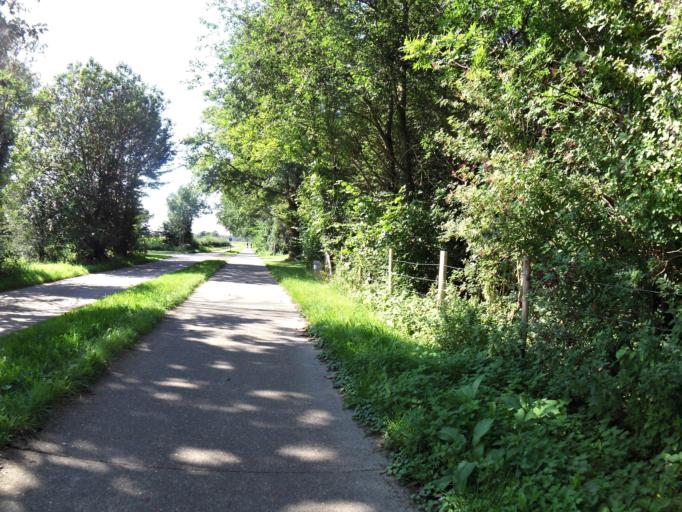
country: BE
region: Flanders
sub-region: Provincie Limburg
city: Tongeren
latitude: 50.7737
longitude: 5.5055
